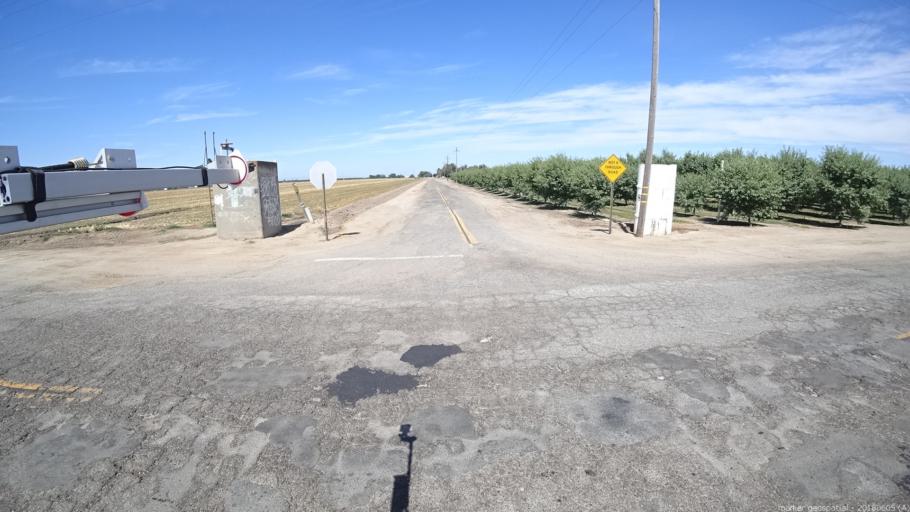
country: US
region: California
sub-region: Madera County
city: Chowchilla
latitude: 37.1199
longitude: -120.3827
